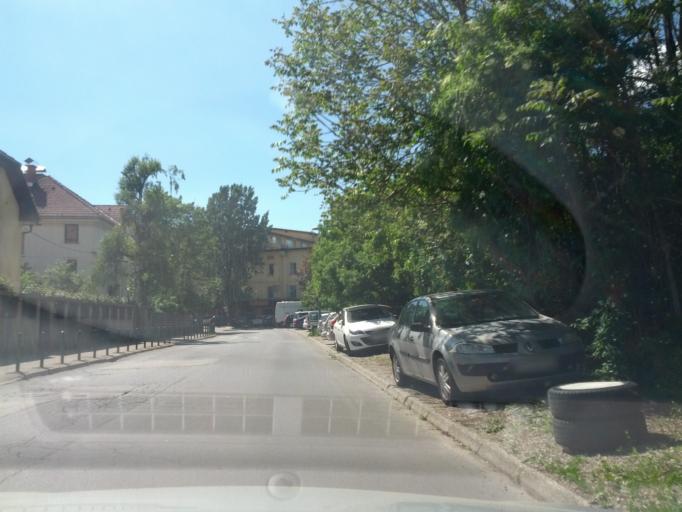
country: SI
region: Ljubljana
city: Ljubljana
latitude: 46.0584
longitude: 14.5232
